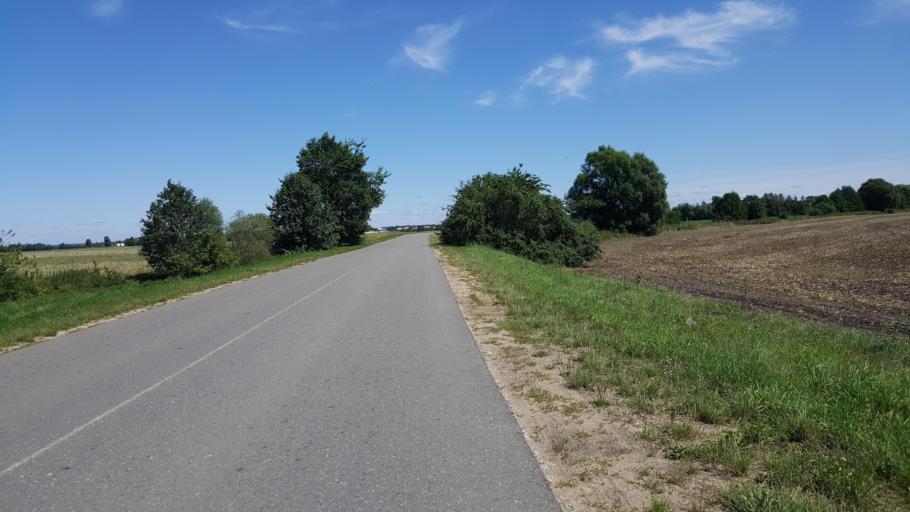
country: BY
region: Brest
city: Charnawchytsy
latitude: 52.2228
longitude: 23.7691
